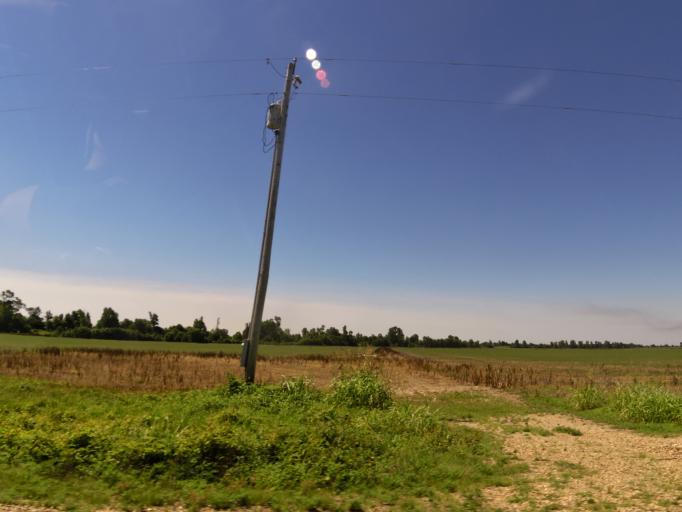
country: US
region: Missouri
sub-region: New Madrid County
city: Lilbourn
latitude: 36.5551
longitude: -89.6743
